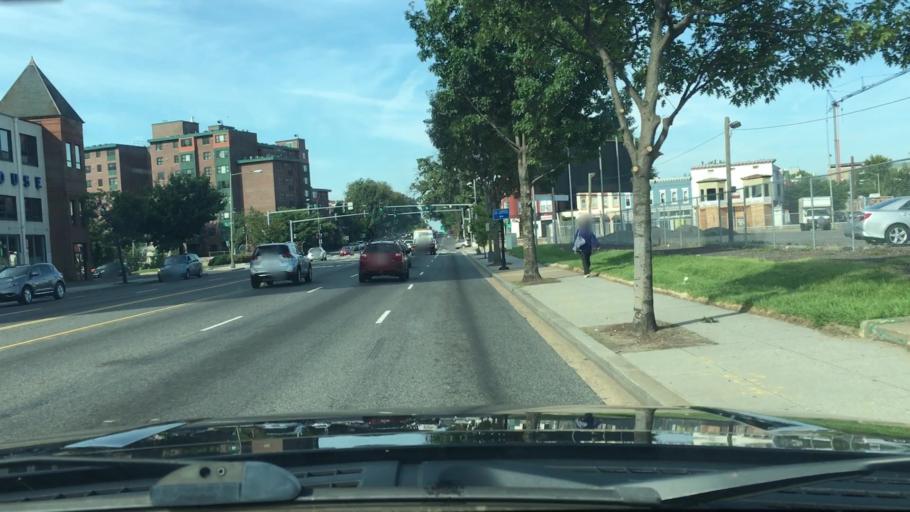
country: US
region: Washington, D.C.
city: Washington, D.C.
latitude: 38.9079
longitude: -77.0078
